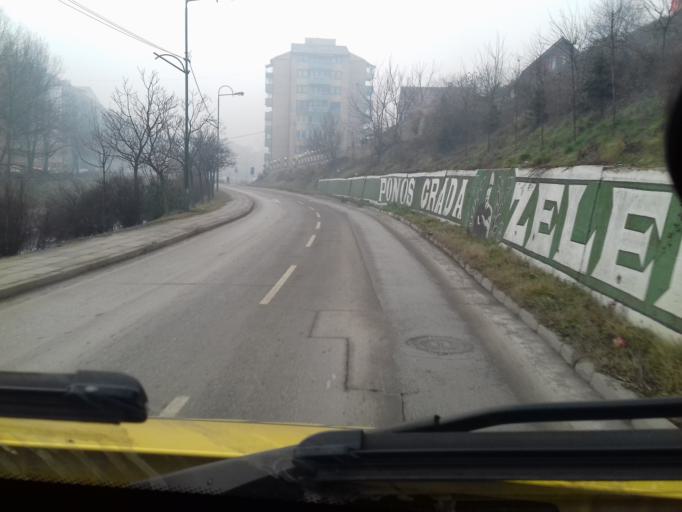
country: BA
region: Federation of Bosnia and Herzegovina
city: Kakanj
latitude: 44.1278
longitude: 18.1158
